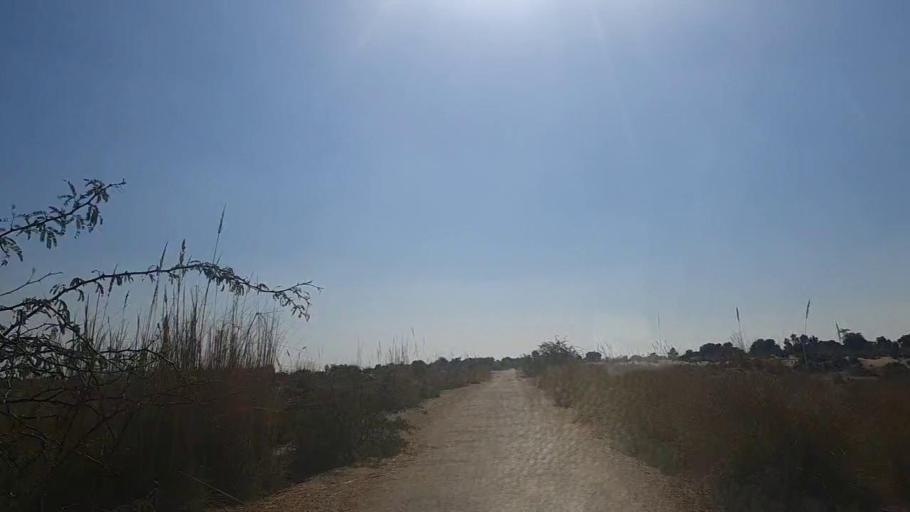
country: PK
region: Sindh
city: Khadro
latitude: 26.1595
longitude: 68.8380
